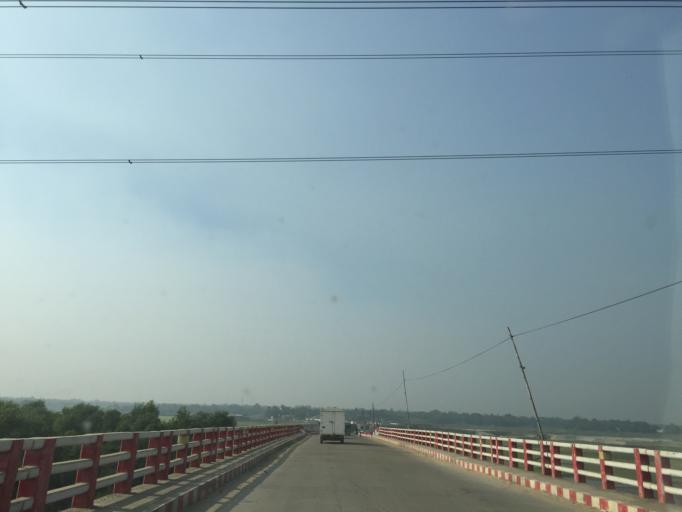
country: BD
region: Dhaka
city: Tungi
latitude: 23.8518
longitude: 90.3387
